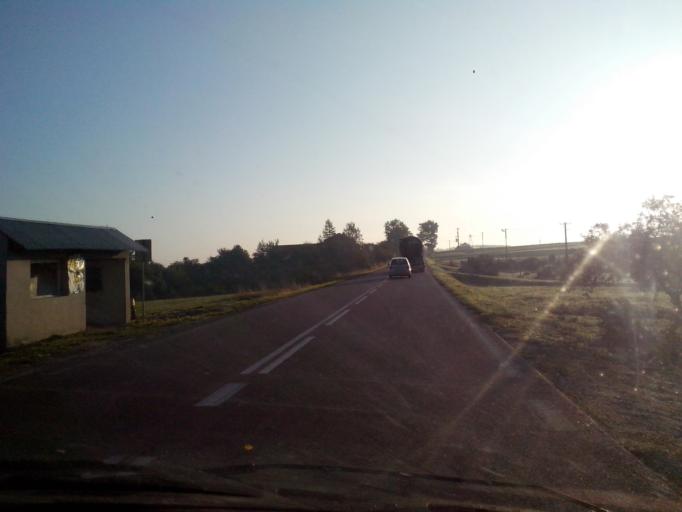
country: PL
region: Subcarpathian Voivodeship
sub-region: Powiat brzozowski
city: Wesola
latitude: 49.8228
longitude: 22.0586
